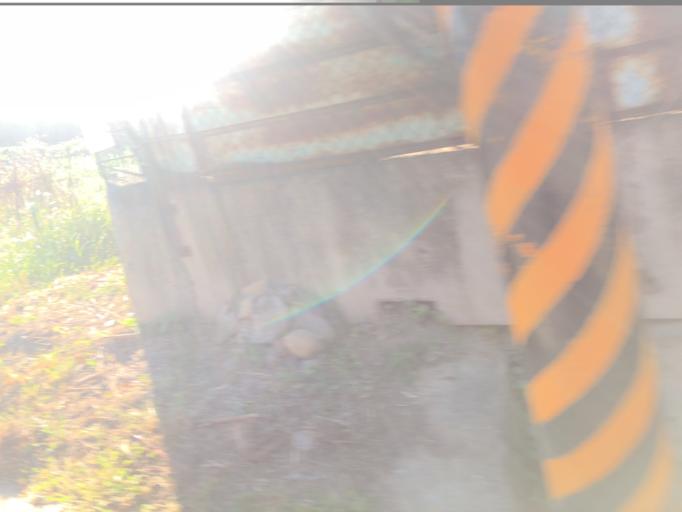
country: TW
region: Taiwan
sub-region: Hsinchu
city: Hsinchu
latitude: 24.7412
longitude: 120.9750
